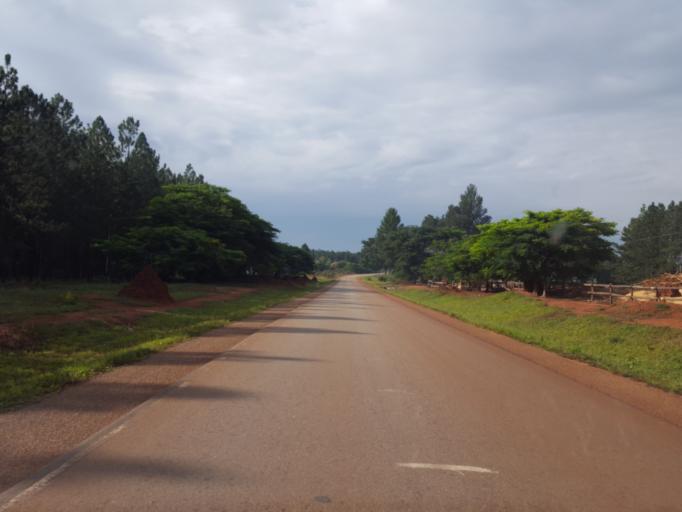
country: UG
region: Central Region
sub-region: Kyankwanzi District
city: Kyankwanzi
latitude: 1.2111
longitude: 31.5585
